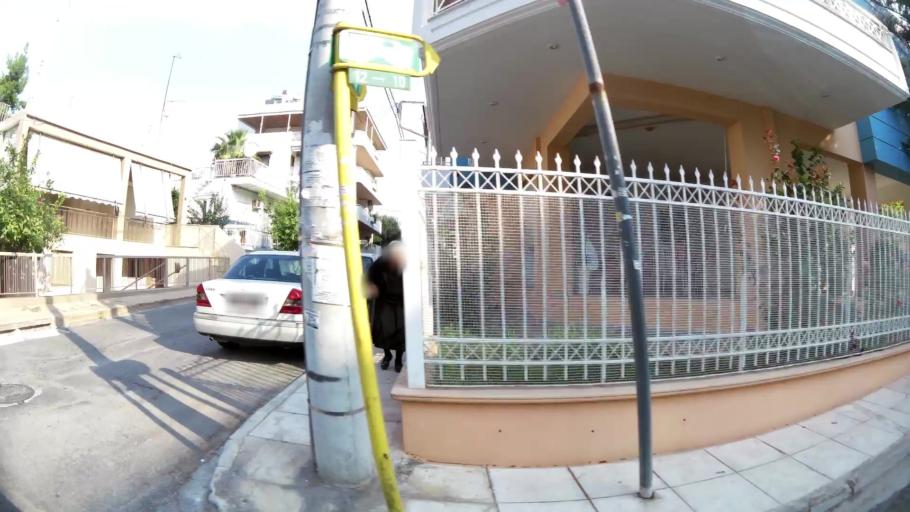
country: GR
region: Attica
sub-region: Nomarchia Athinas
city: Agios Dimitrios
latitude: 37.9321
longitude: 23.7199
